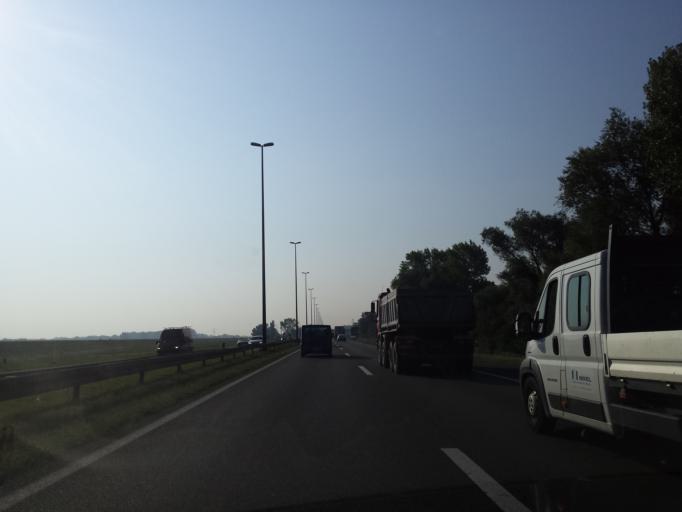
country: HR
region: Grad Zagreb
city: Lucko
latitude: 45.7790
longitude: 15.8710
